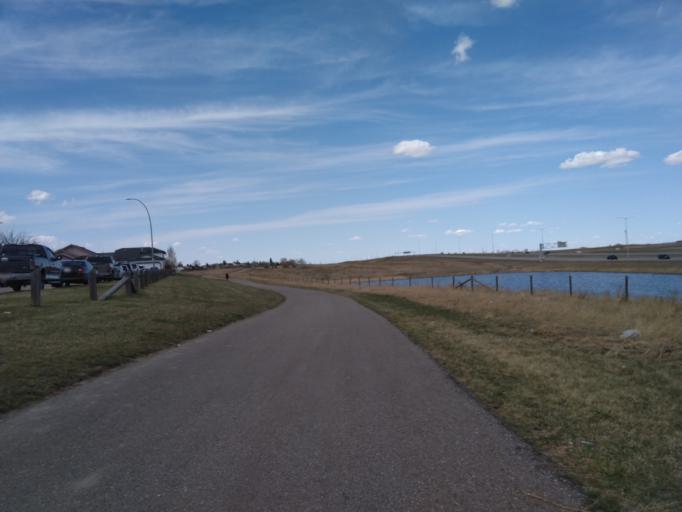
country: CA
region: Alberta
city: Chestermere
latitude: 51.0488
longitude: -113.9229
